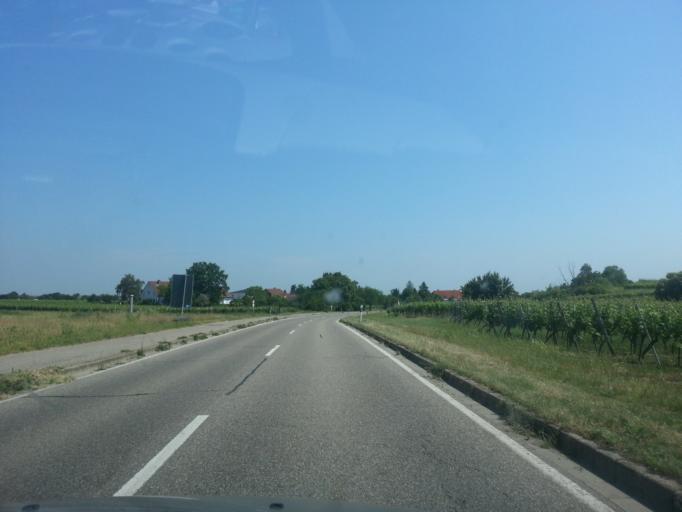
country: DE
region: Rheinland-Pfalz
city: Freinsheim
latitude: 49.4977
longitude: 8.1992
